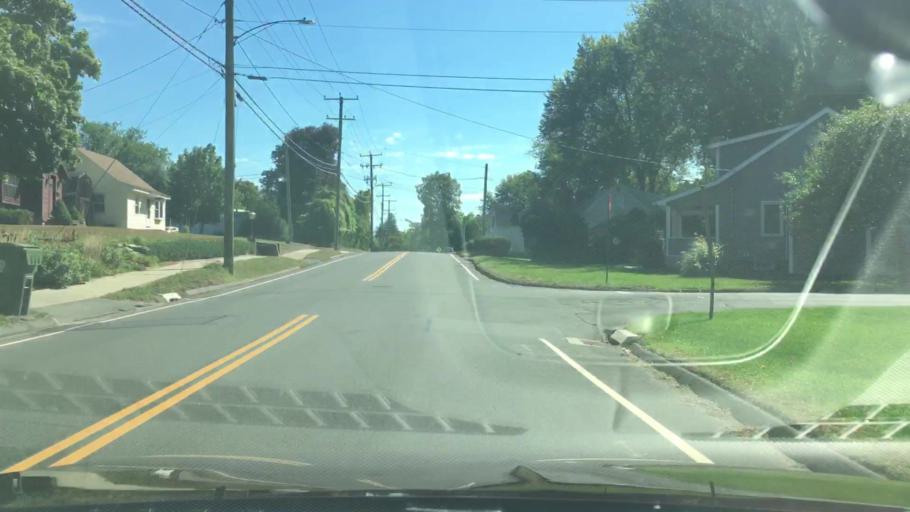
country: US
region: Connecticut
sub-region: Hartford County
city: Bristol
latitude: 41.6831
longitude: -72.9080
